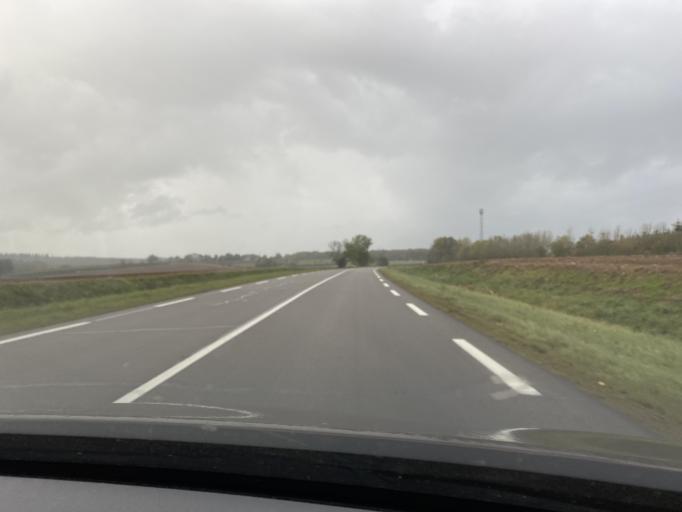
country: FR
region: Bourgogne
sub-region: Departement de la Cote-d'Or
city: Saulieu
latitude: 47.3176
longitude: 4.1955
